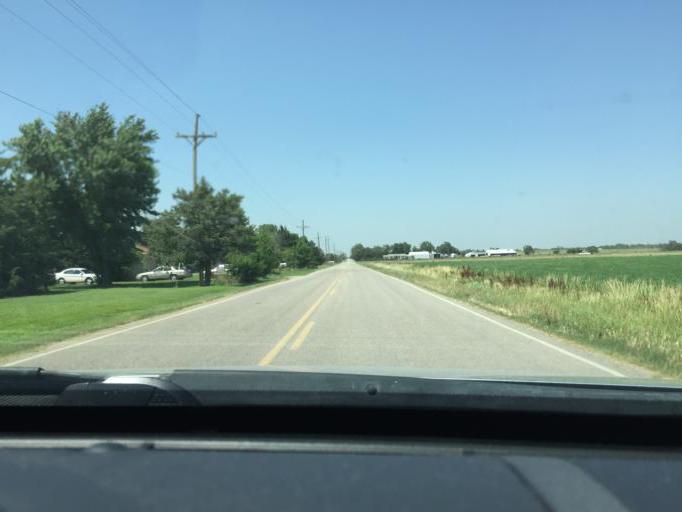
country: US
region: Kansas
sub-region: Reno County
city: Haven
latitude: 37.9266
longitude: -97.8853
